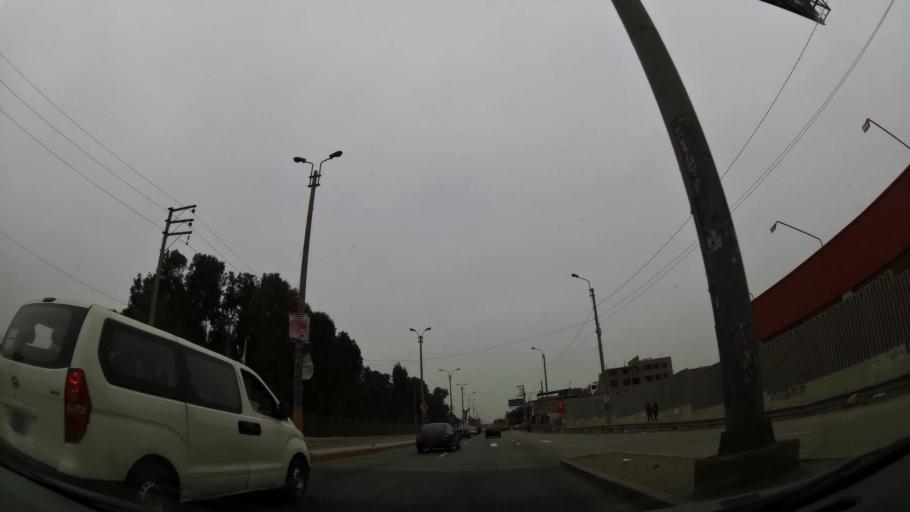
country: PE
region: Lima
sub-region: Lima
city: Surco
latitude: -12.1928
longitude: -76.9704
